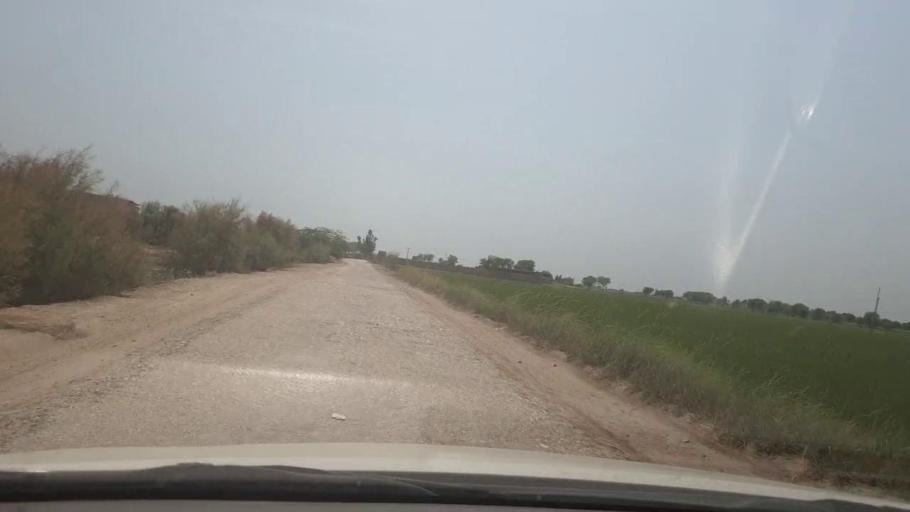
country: PK
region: Sindh
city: Shikarpur
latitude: 27.9952
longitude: 68.5851
